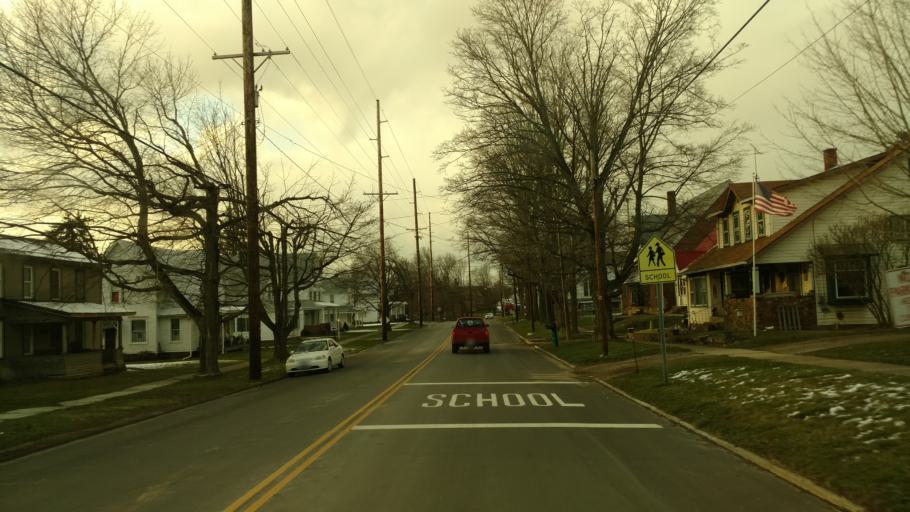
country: US
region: Ohio
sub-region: Ashland County
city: Ashland
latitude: 40.8047
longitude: -82.1959
